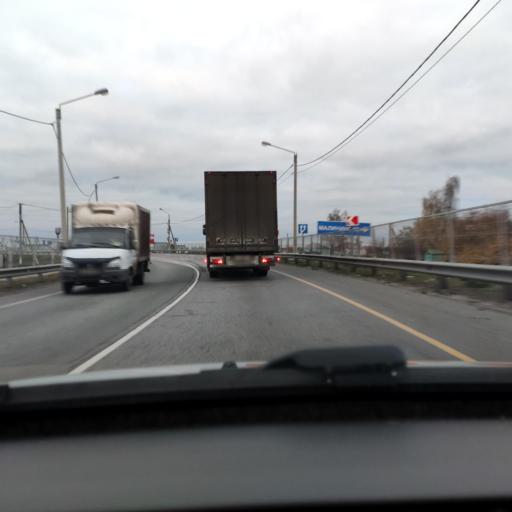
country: RU
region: Lipetsk
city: Khlevnoye
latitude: 52.2661
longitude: 39.1674
